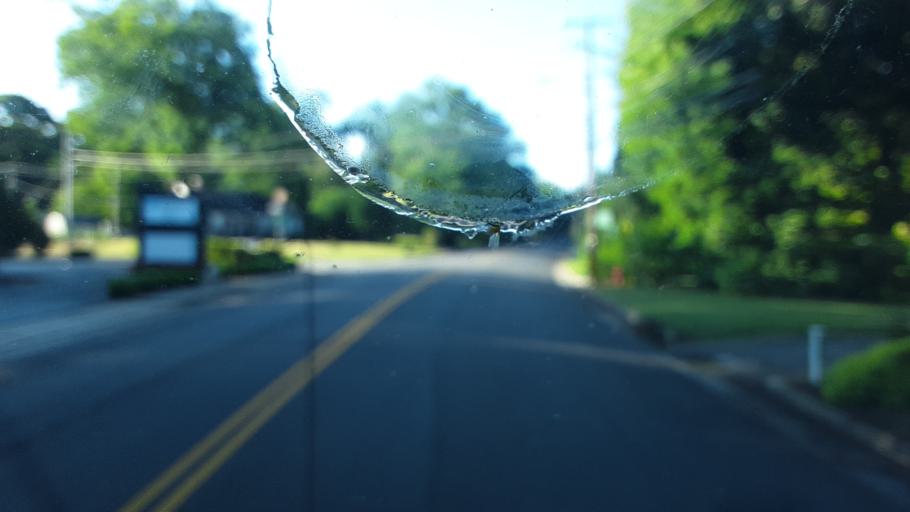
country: US
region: Virginia
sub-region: Pittsylvania County
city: Chatham
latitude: 36.8146
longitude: -79.3954
